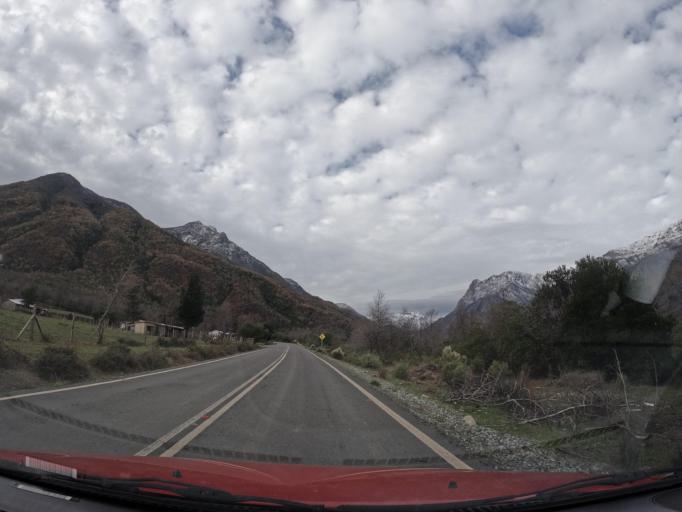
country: CL
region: Maule
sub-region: Provincia de Linares
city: Colbun
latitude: -35.8596
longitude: -71.2494
